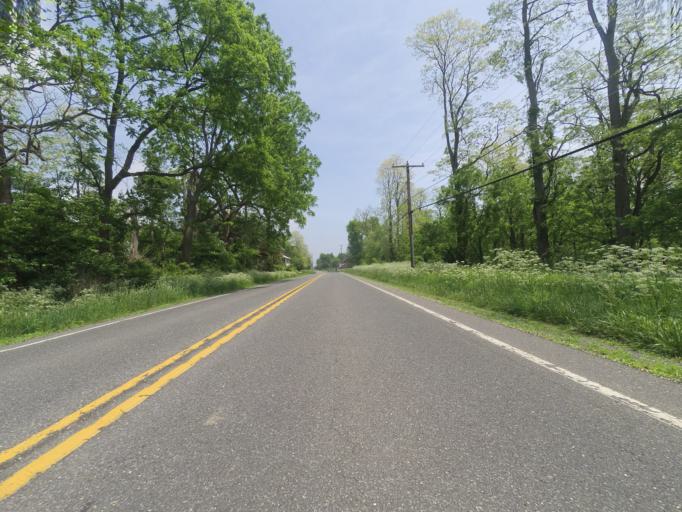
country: US
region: Pennsylvania
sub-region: Centre County
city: Pine Grove Mills
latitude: 40.7068
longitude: -77.9719
